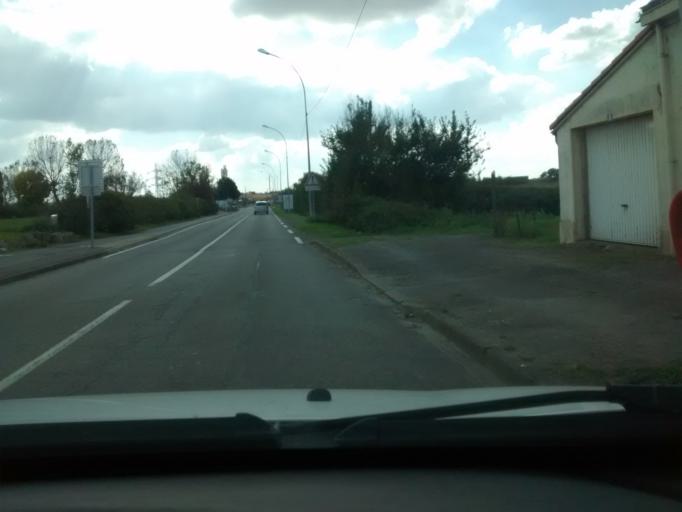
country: FR
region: Pays de la Loire
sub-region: Departement de la Loire-Atlantique
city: Saint-Paimboeuf
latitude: 47.2823
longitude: -2.0158
